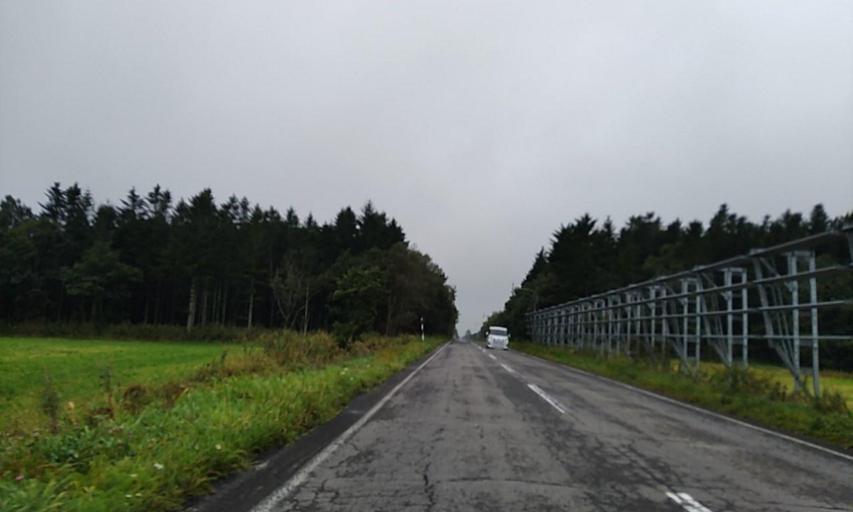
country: JP
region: Hokkaido
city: Shibetsu
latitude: 43.5292
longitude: 144.6982
